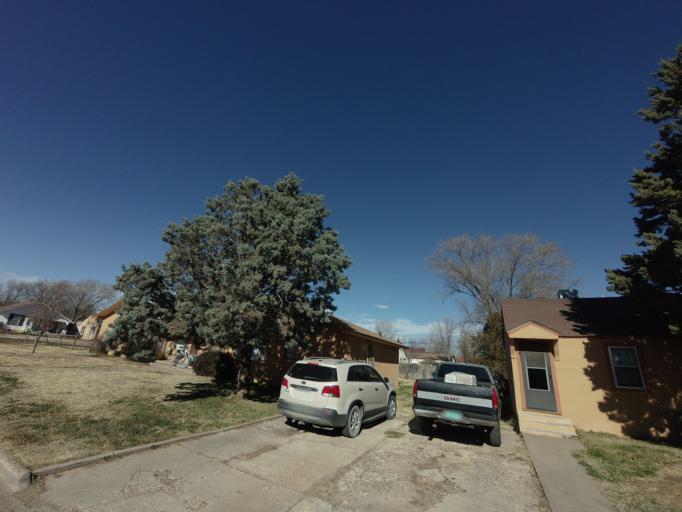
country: US
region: New Mexico
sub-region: Curry County
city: Clovis
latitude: 34.4110
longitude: -103.2100
